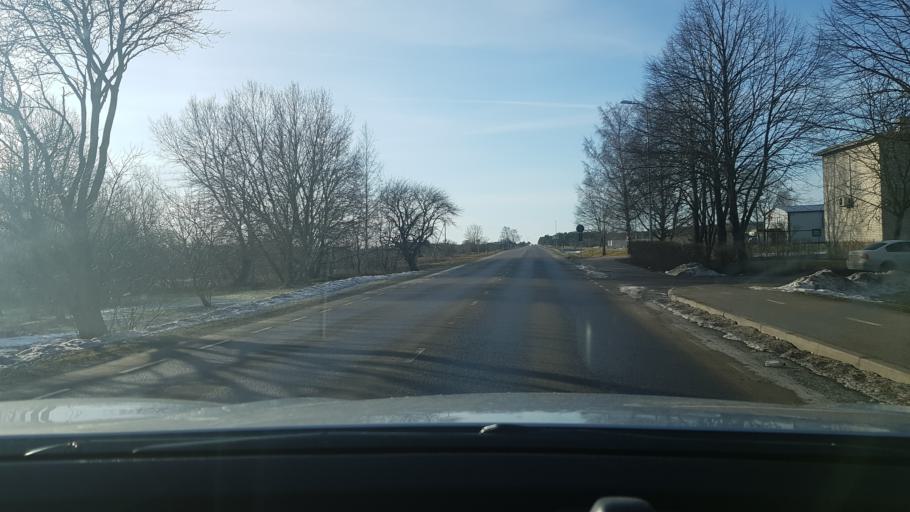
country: EE
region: Saare
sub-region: Kuressaare linn
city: Kuressaare
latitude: 58.2529
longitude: 22.5092
